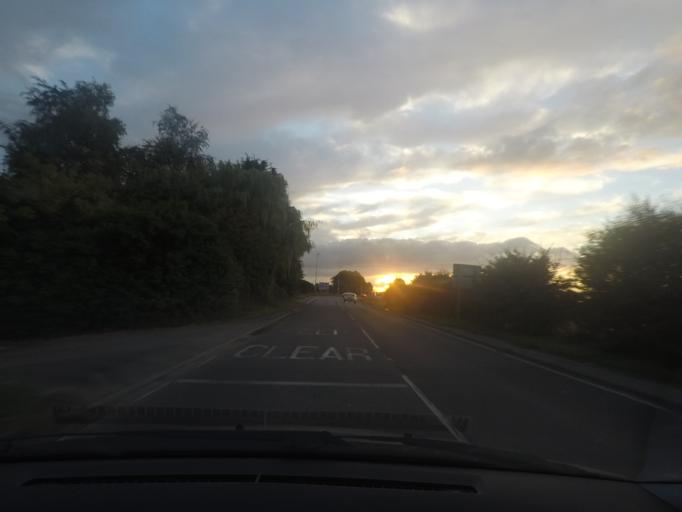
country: GB
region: England
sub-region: North Lincolnshire
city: Barnetby le Wold
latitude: 53.5822
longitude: -0.4076
